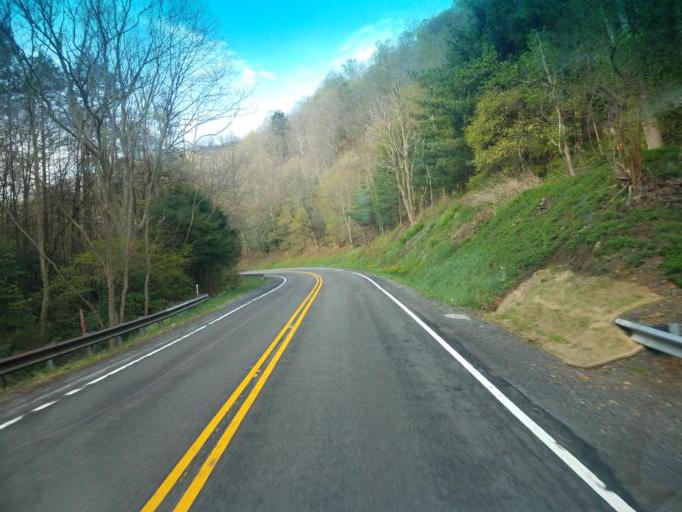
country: US
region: Virginia
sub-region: Smyth County
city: Atkins
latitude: 36.8035
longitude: -81.4040
